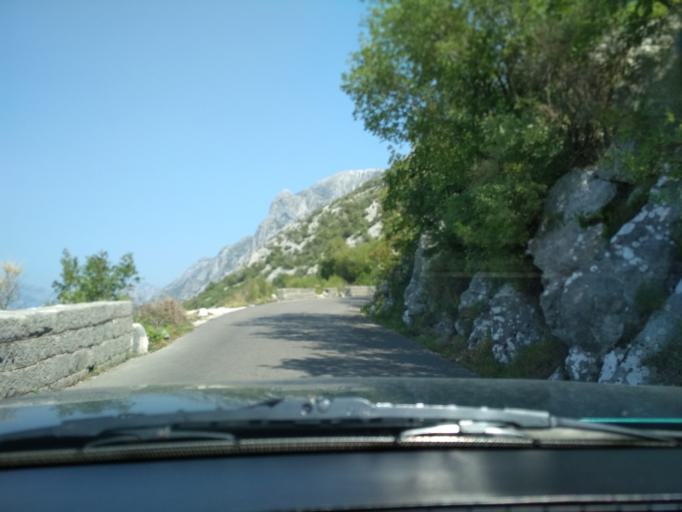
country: ME
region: Kotor
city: Kotor
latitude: 42.4116
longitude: 18.7794
